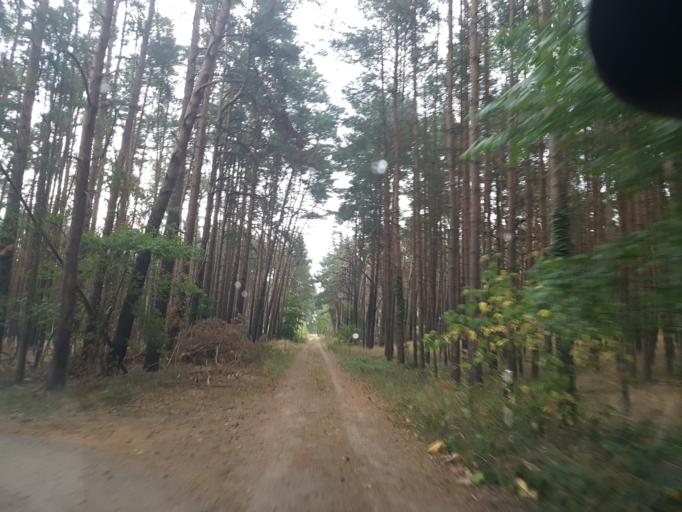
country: DE
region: Brandenburg
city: Bad Liebenwerda
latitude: 51.5520
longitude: 13.3726
